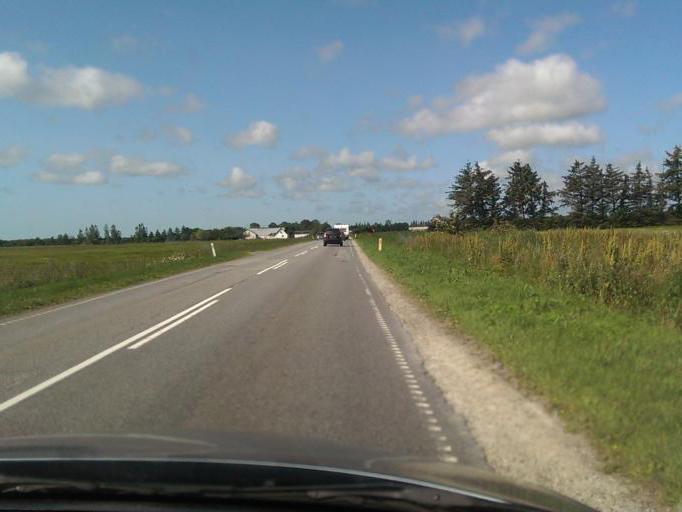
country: DK
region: North Denmark
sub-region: Bronderslev Kommune
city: Bronderslev
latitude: 57.2094
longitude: 9.8917
